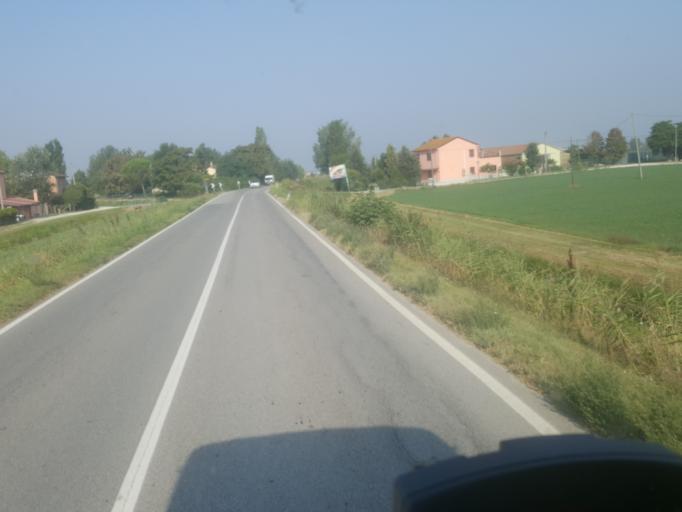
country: IT
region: Emilia-Romagna
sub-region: Provincia di Ravenna
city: Voltana
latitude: 44.5609
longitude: 11.9101
